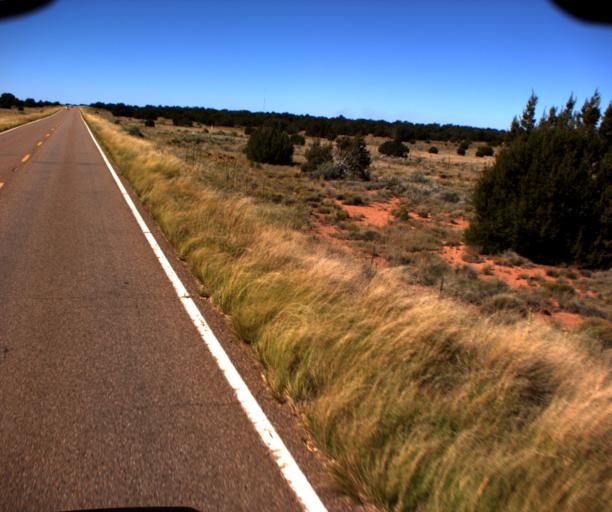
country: US
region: Arizona
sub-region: Navajo County
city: Heber-Overgaard
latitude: 34.4665
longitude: -110.3728
